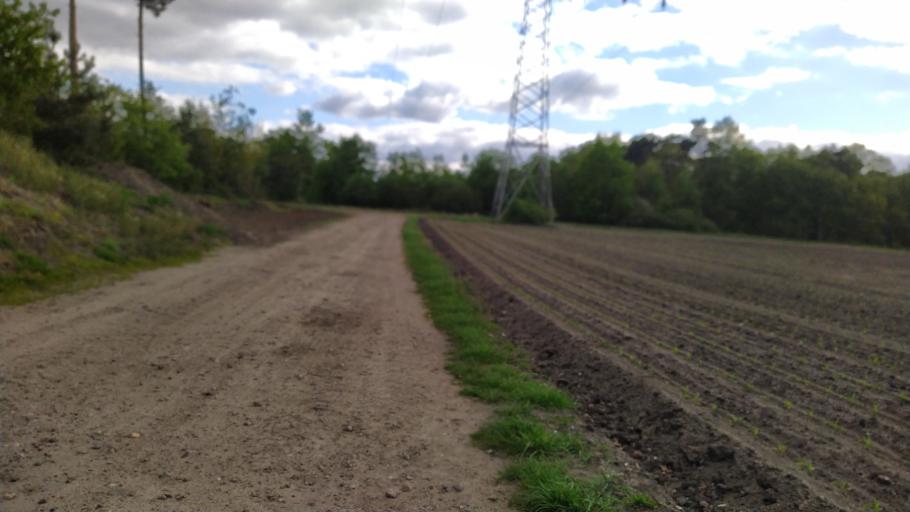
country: DE
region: Lower Saxony
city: Brest
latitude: 53.4331
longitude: 9.3933
